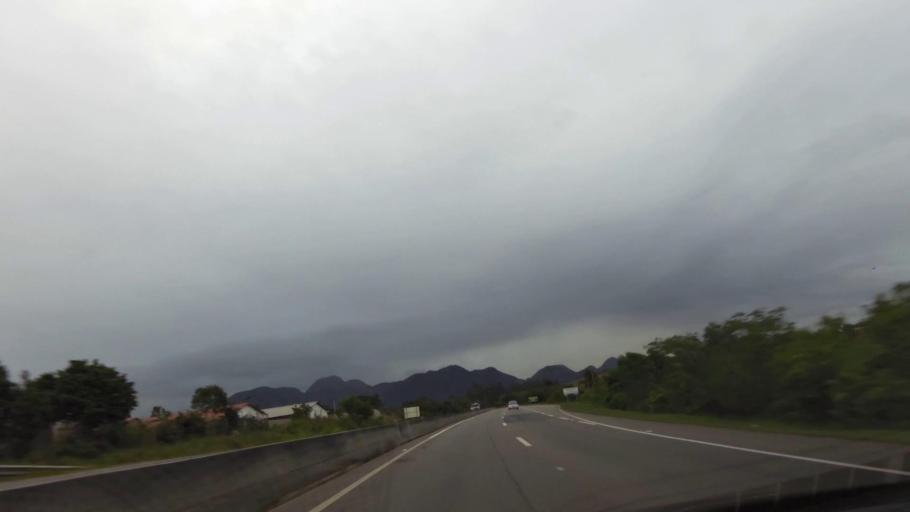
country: BR
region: Espirito Santo
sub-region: Guarapari
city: Guarapari
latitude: -20.6135
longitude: -40.4548
